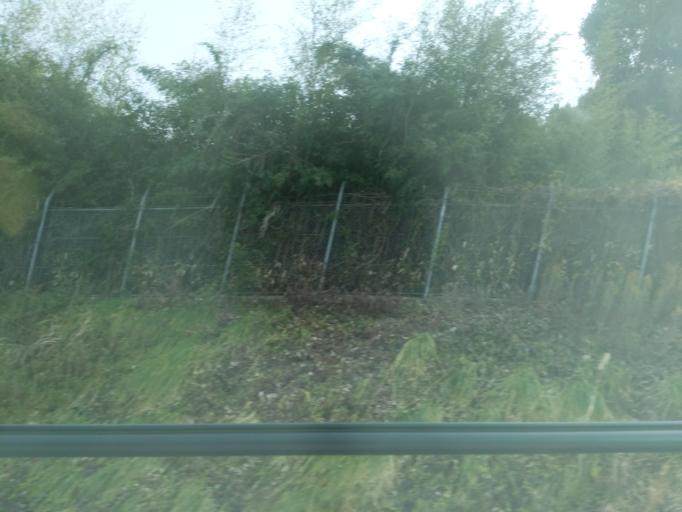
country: JP
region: Miyagi
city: Kogota
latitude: 38.7023
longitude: 141.0454
